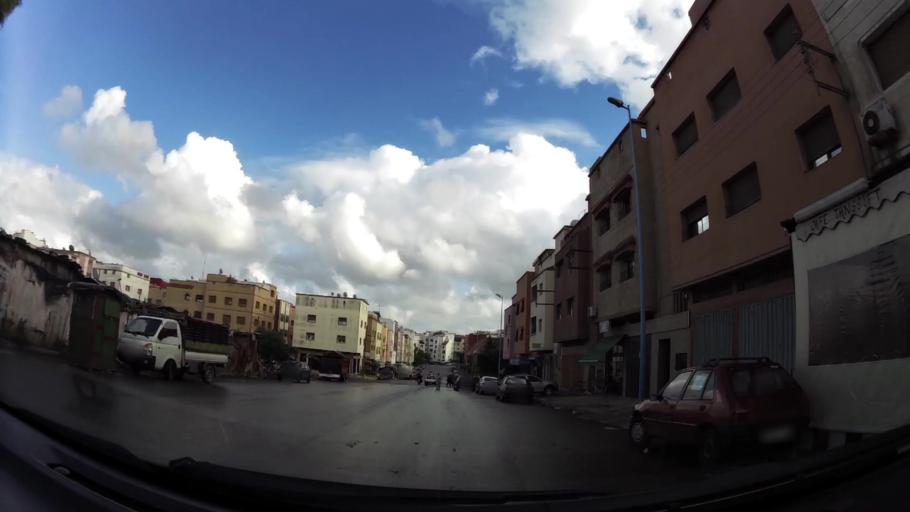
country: MA
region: Grand Casablanca
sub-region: Casablanca
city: Casablanca
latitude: 33.5441
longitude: -7.5912
